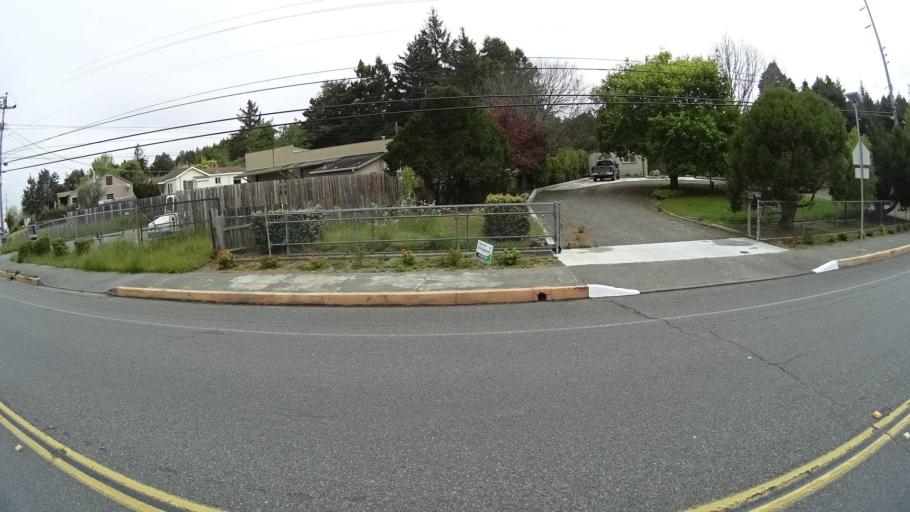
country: US
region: California
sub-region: Humboldt County
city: Cutten
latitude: 40.7708
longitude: -124.1611
